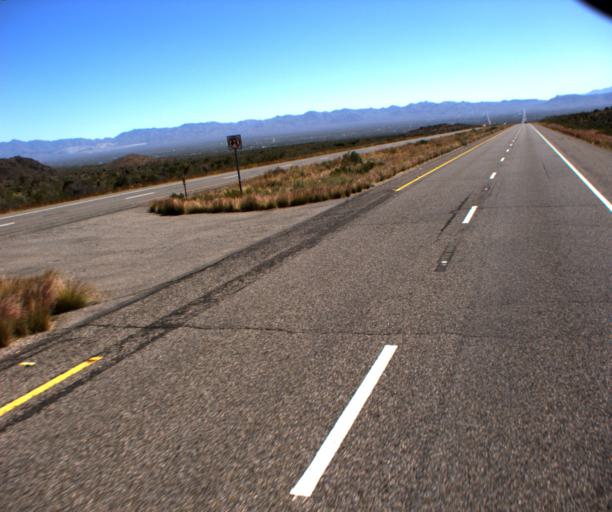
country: US
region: Arizona
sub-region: Mohave County
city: Golden Valley
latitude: 35.2291
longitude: -114.3667
